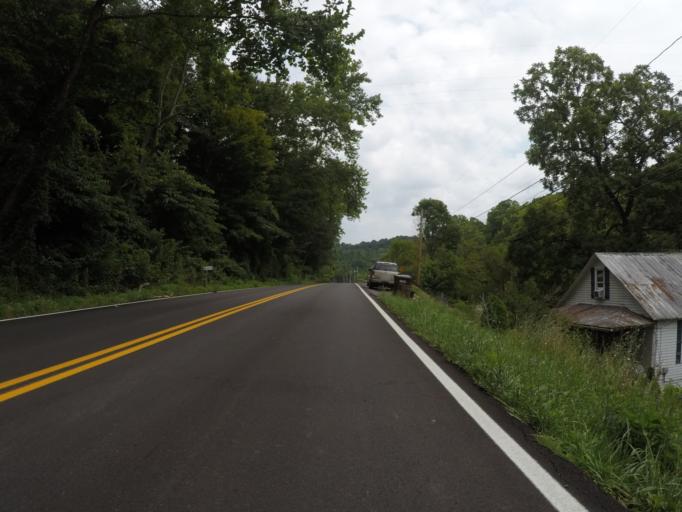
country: US
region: Kentucky
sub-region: Boyd County
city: Catlettsburg
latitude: 38.4193
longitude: -82.6168
